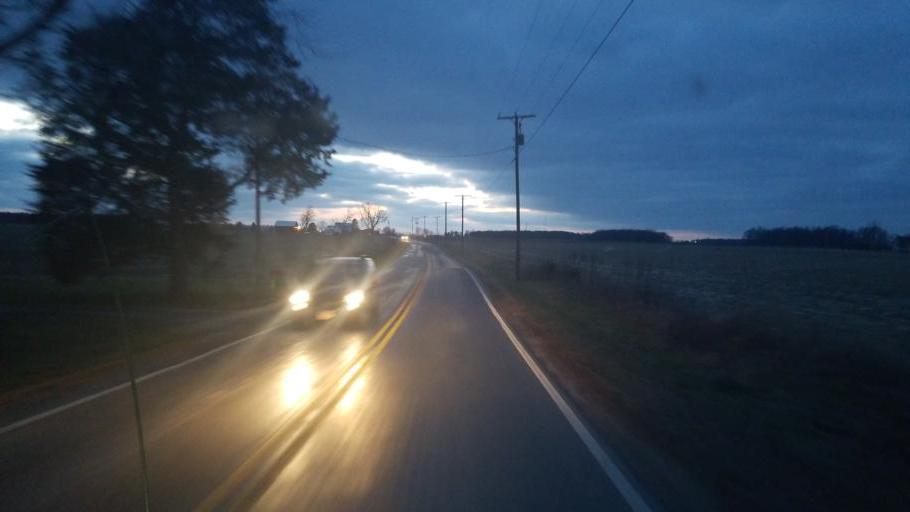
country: US
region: Ohio
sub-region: Marion County
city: Prospect
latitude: 40.4348
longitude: -83.0874
